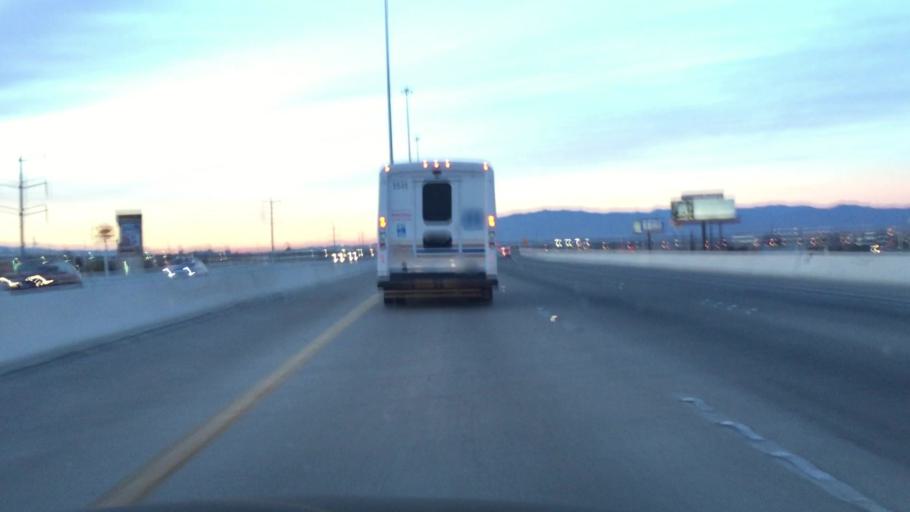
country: US
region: Nevada
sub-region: Clark County
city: Henderson
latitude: 36.0585
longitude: -115.0286
